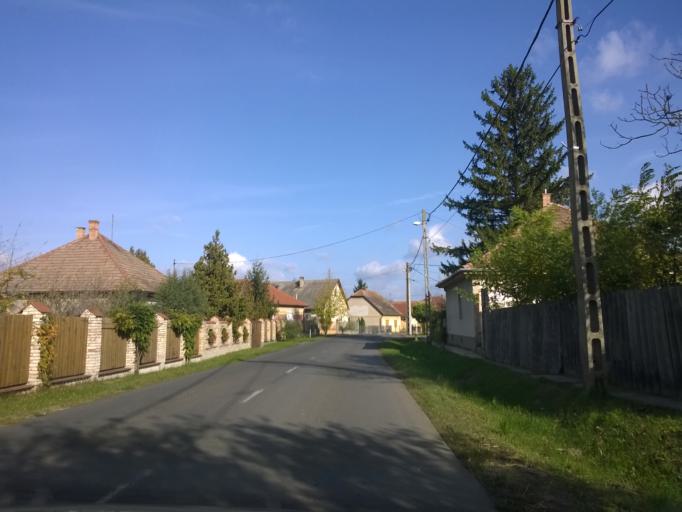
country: HU
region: Pest
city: Rackeve
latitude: 47.1258
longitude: 18.9471
